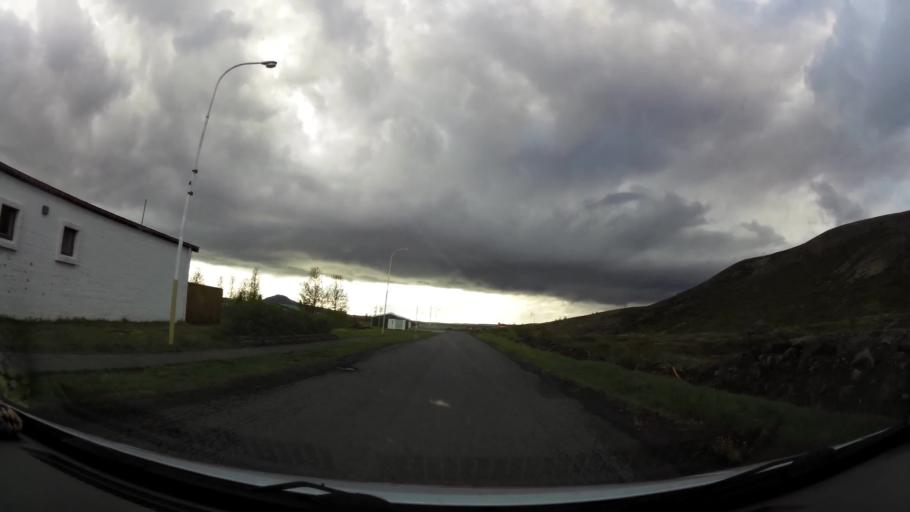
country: IS
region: Northeast
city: Laugar
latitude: 65.6424
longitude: -16.9030
